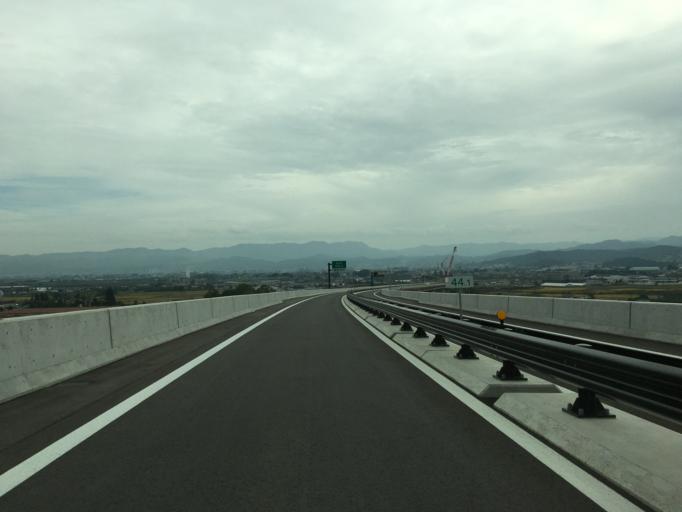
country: JP
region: Fukushima
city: Hobaramachi
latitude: 37.8325
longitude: 140.5015
